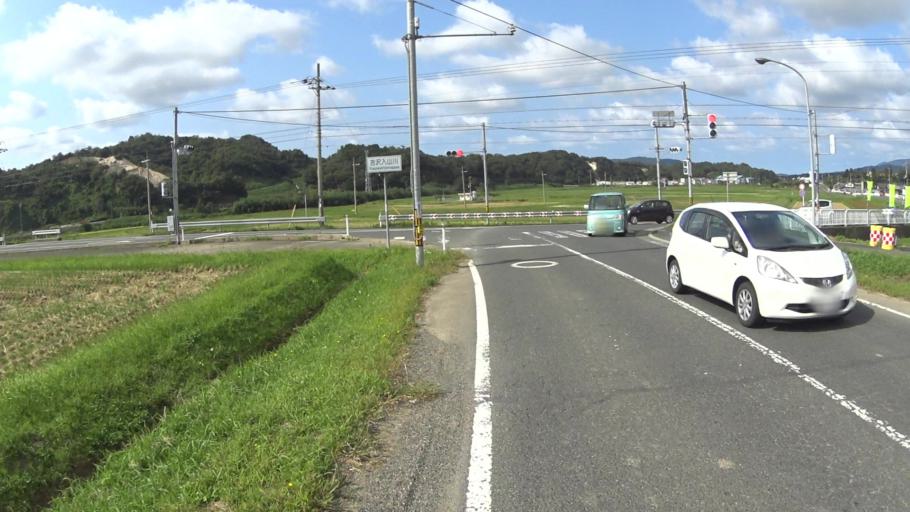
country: JP
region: Kyoto
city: Miyazu
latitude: 35.6423
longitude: 135.0879
